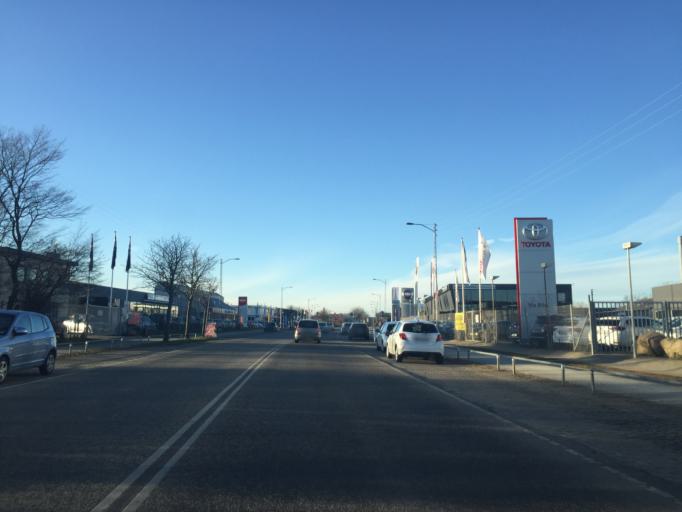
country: DK
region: Capital Region
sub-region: Tarnby Kommune
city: Tarnby
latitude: 55.6201
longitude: 12.6051
